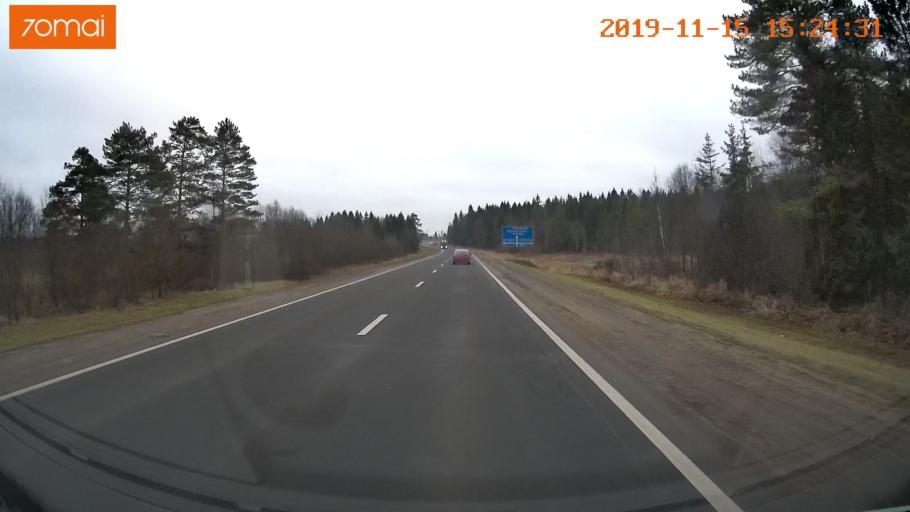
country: RU
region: Jaroslavl
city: Danilov
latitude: 58.1766
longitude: 40.1330
